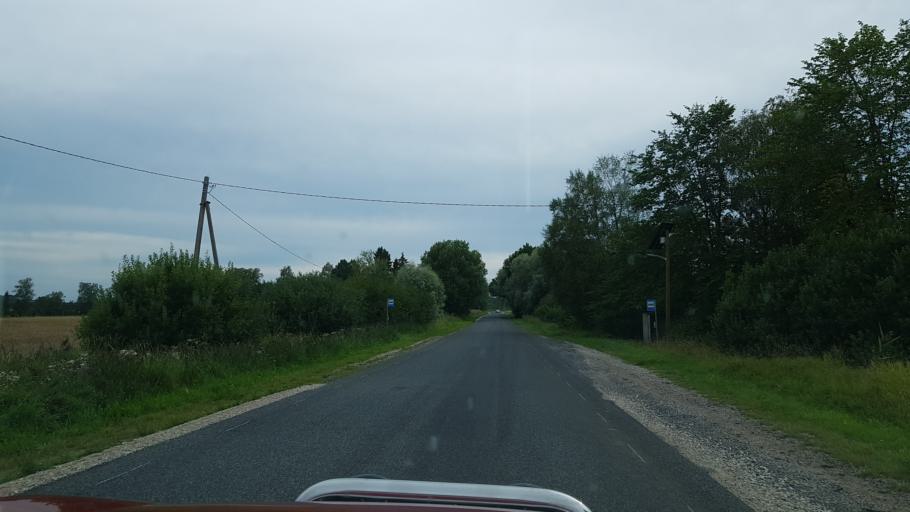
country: EE
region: Laeaene
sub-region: Lihula vald
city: Lihula
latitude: 58.8787
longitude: 23.8528
